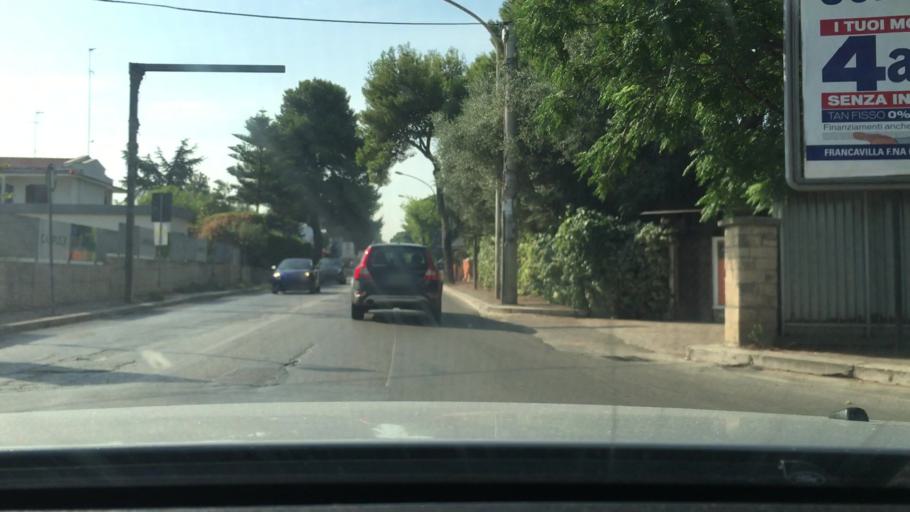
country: IT
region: Apulia
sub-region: Provincia di Bari
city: Bari
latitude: 41.0981
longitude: 16.8897
